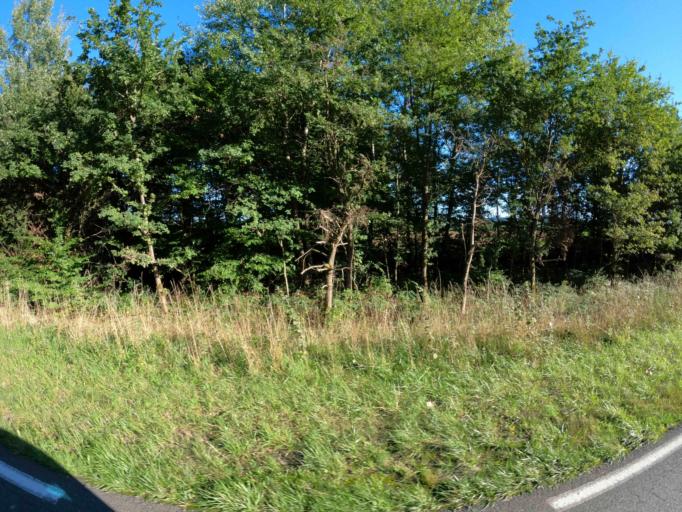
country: FR
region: Bourgogne
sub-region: Departement de Saone-et-Loire
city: Blanzy
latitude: 46.7110
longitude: 4.4202
